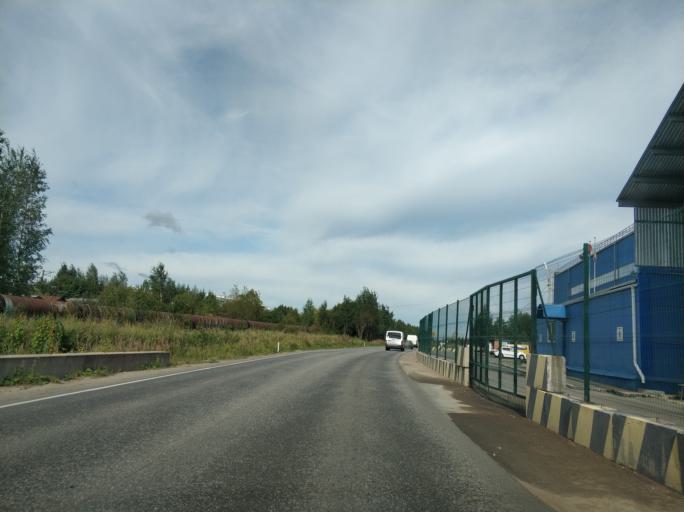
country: RU
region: St.-Petersburg
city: Grazhdanka
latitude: 60.0482
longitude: 30.4098
